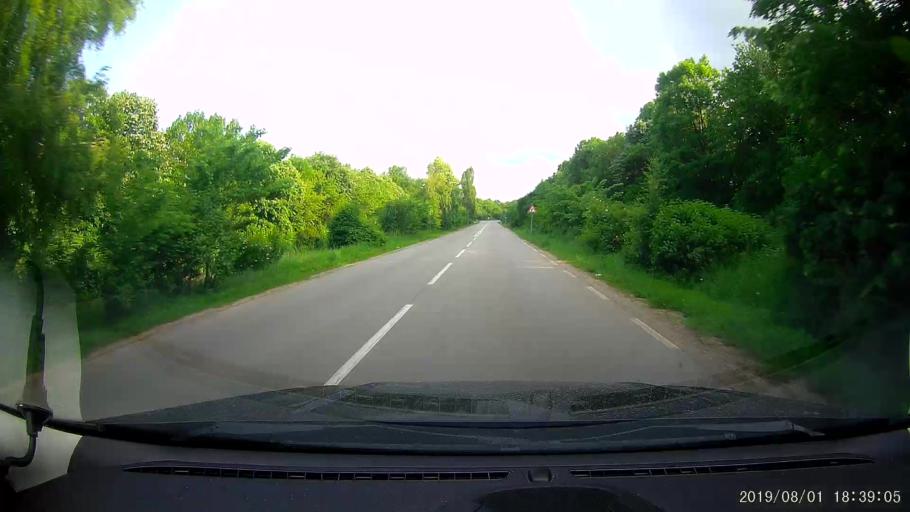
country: BG
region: Shumen
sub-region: Obshtina Khitrino
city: Gara Khitrino
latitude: 43.3928
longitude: 26.9173
